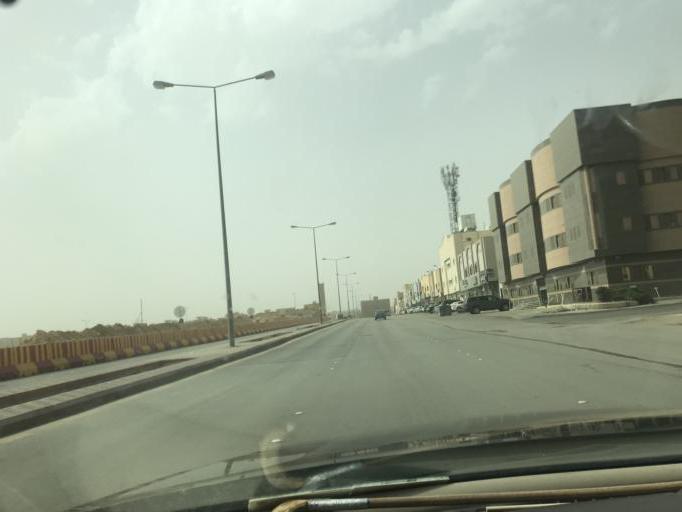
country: SA
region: Ar Riyad
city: Riyadh
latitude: 24.7962
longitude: 46.6675
